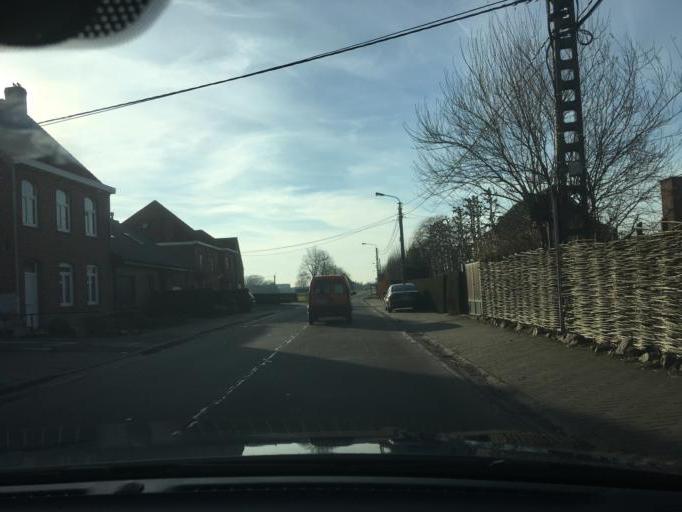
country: BE
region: Flanders
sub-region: Provincie West-Vlaanderen
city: Wielsbeke
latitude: 50.9250
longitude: 3.3864
